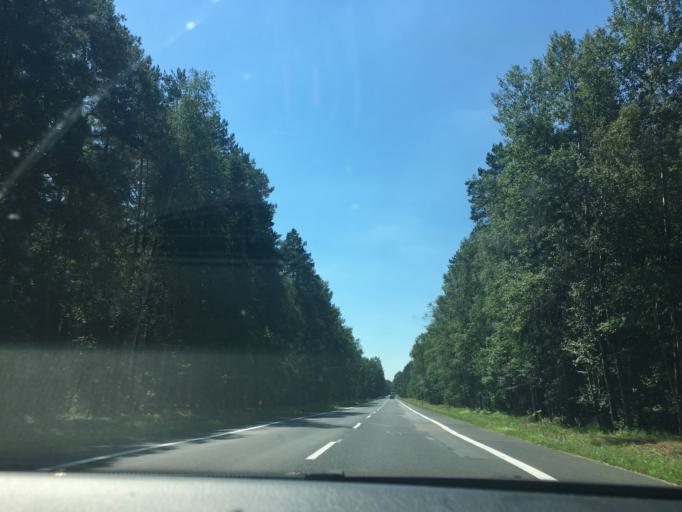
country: PL
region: Subcarpathian Voivodeship
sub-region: Powiat nizanski
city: Jarocin
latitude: 50.5880
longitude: 22.2769
